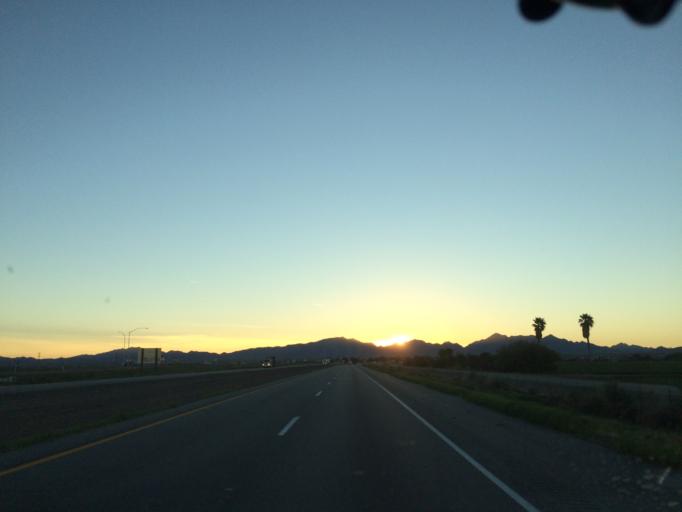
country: US
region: Arizona
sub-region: La Paz County
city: Ehrenberg
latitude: 33.6077
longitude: -114.5506
